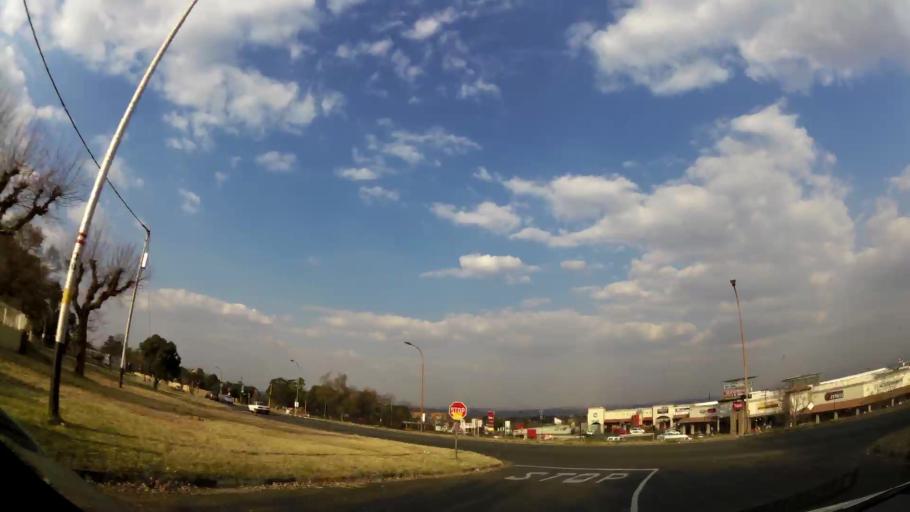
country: ZA
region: Gauteng
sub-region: Ekurhuleni Metropolitan Municipality
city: Germiston
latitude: -26.2458
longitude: 28.1785
